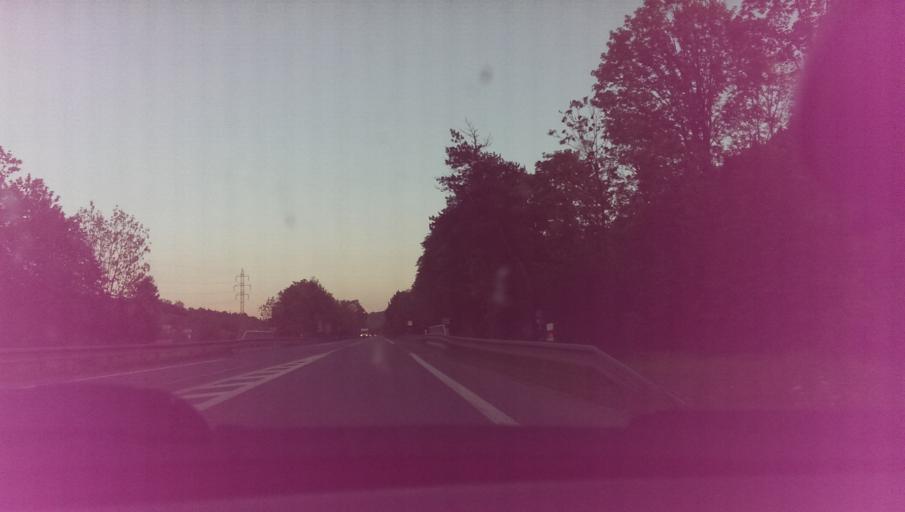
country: CZ
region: Zlin
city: Jablunka
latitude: 49.3592
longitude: 17.9644
